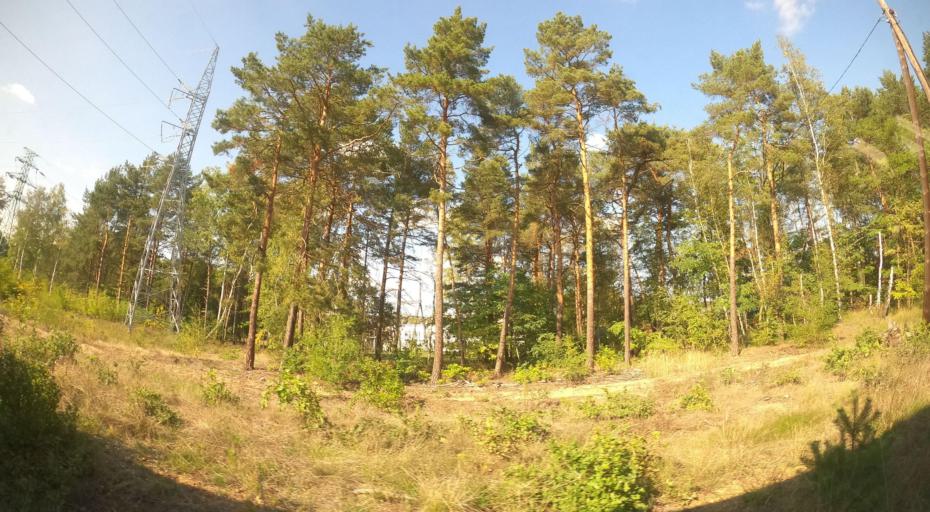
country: PL
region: Lubusz
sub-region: Zielona Gora
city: Zielona Gora
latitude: 51.9406
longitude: 15.4479
